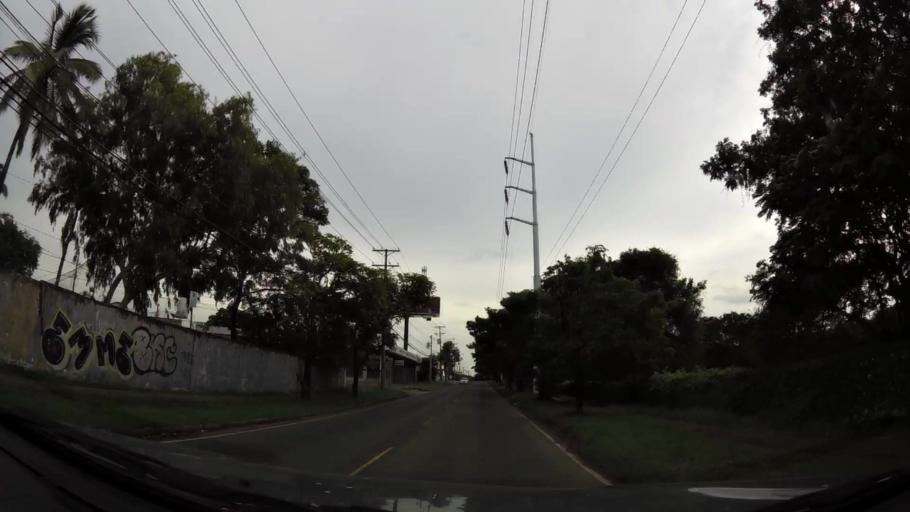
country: PA
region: Panama
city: Panama
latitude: 9.0124
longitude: -79.4929
